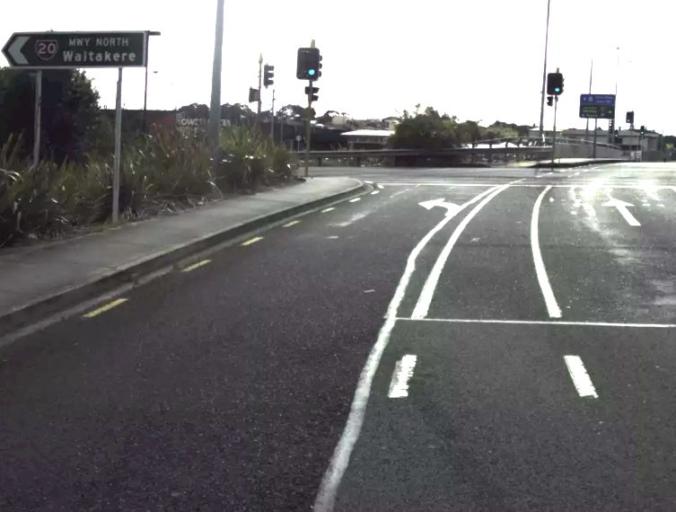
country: NZ
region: Auckland
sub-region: Auckland
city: Auckland
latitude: -36.9183
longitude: 174.7579
